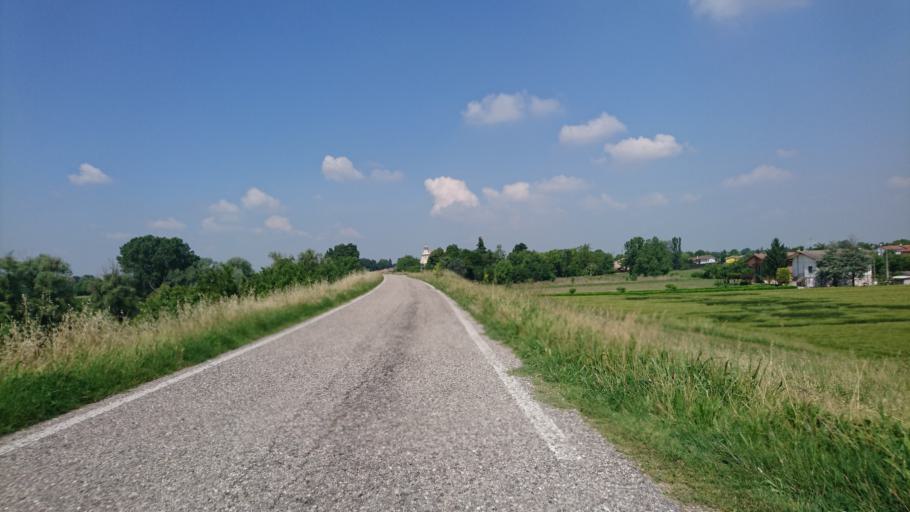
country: IT
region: Lombardy
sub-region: Provincia di Mantova
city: San Benedetto Po
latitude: 45.0803
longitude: 10.9666
